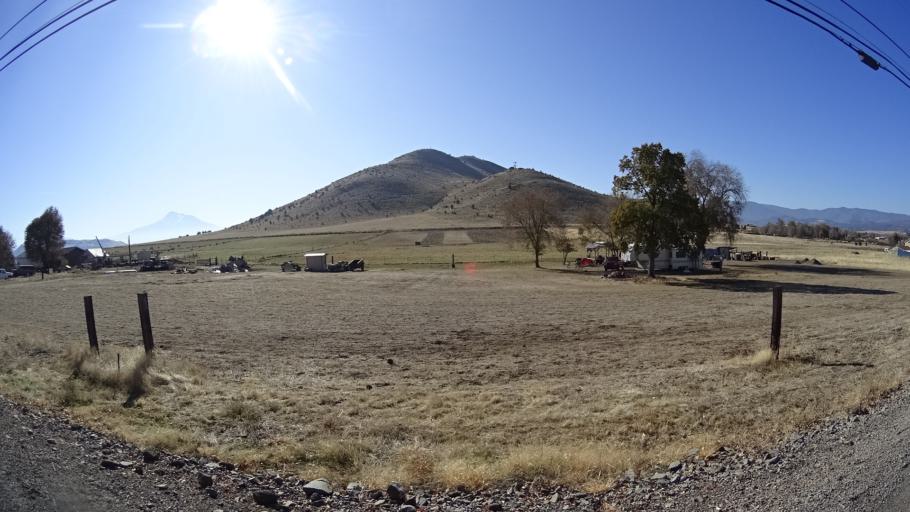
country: US
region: California
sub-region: Siskiyou County
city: Montague
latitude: 41.7248
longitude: -122.5148
